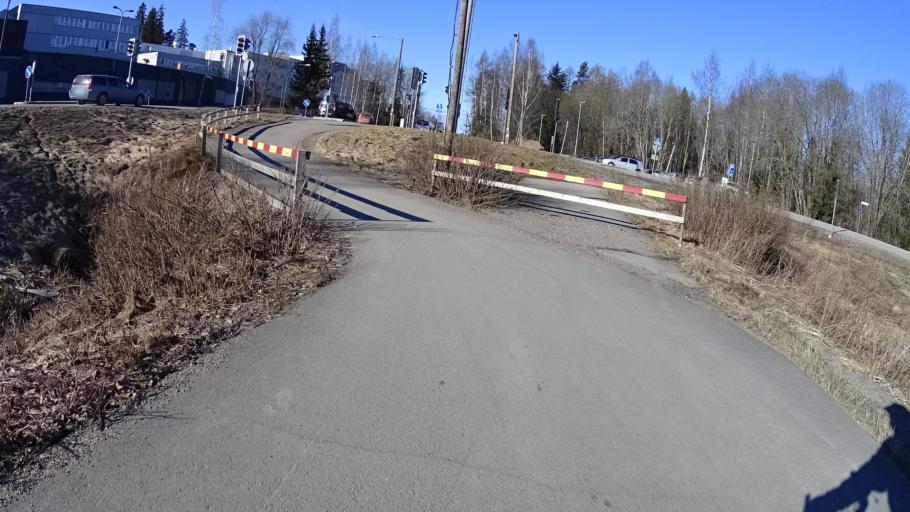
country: FI
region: Uusimaa
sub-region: Helsinki
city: Kauniainen
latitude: 60.2237
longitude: 24.6894
